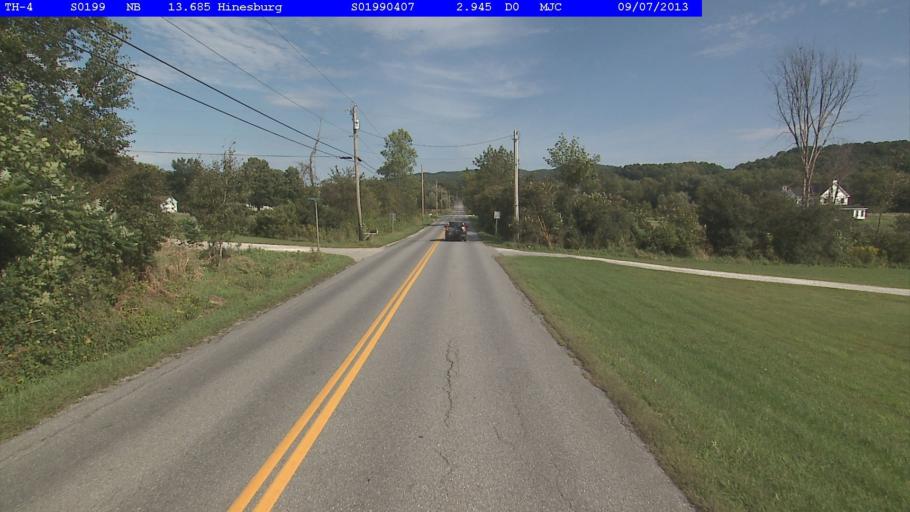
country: US
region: Vermont
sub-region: Chittenden County
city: Hinesburg
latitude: 44.3203
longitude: -73.1100
